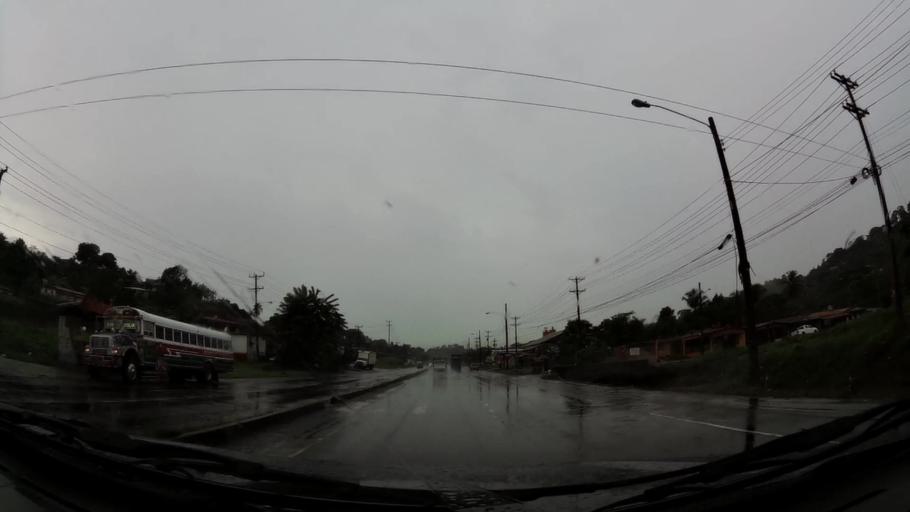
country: PA
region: Colon
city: Cativa
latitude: 9.3592
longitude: -79.8220
